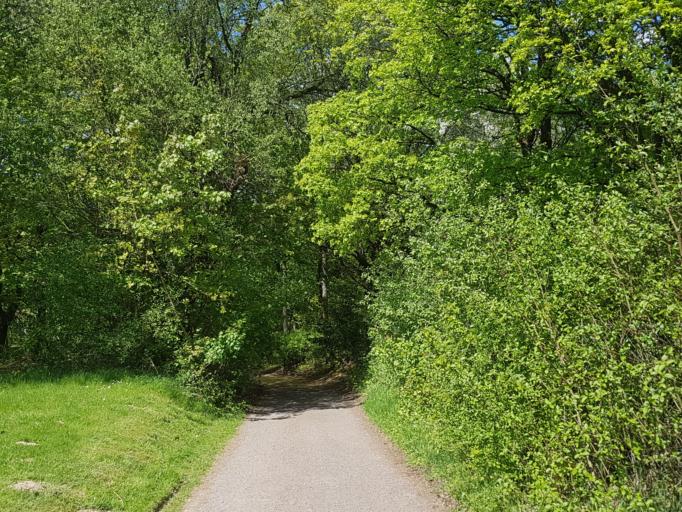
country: DE
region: North Rhine-Westphalia
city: Waldbrol
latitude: 50.8770
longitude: 7.6283
